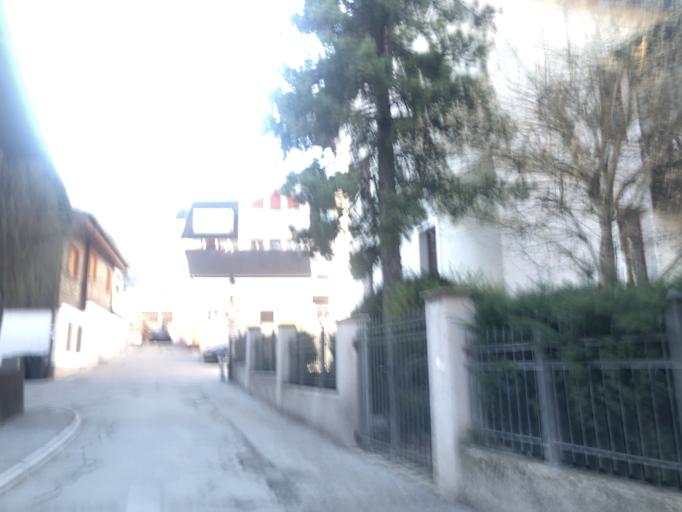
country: AT
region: Styria
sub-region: Politischer Bezirk Liezen
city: Schladming
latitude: 47.3920
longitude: 13.6860
